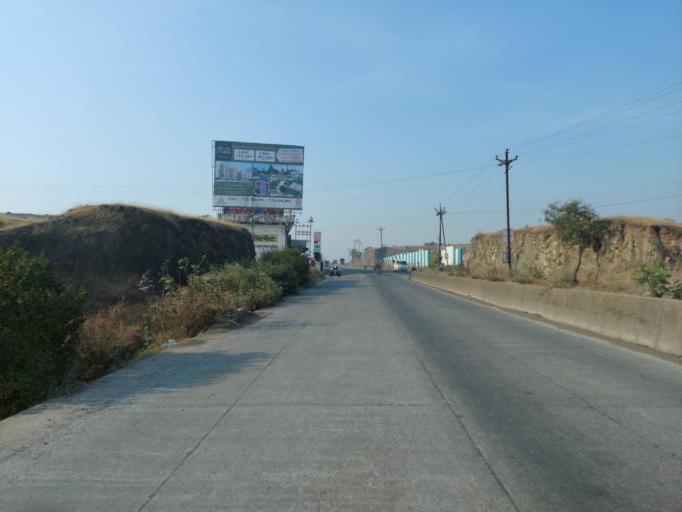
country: IN
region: Maharashtra
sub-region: Pune Division
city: Pune
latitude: 18.4607
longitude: 73.9495
